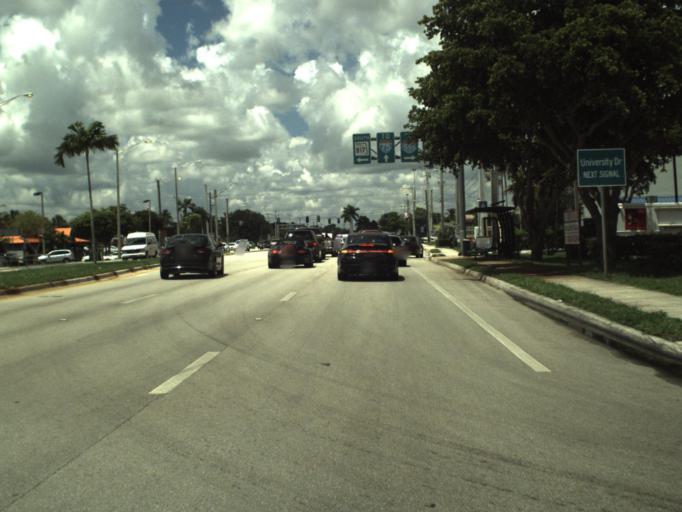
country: US
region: Florida
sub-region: Broward County
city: Pembroke Pines
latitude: 26.0093
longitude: -80.2459
